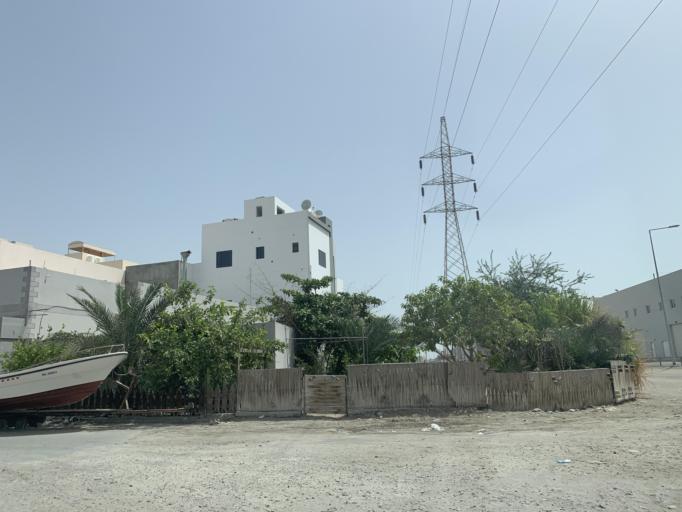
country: BH
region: Northern
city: Sitrah
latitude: 26.1344
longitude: 50.6036
